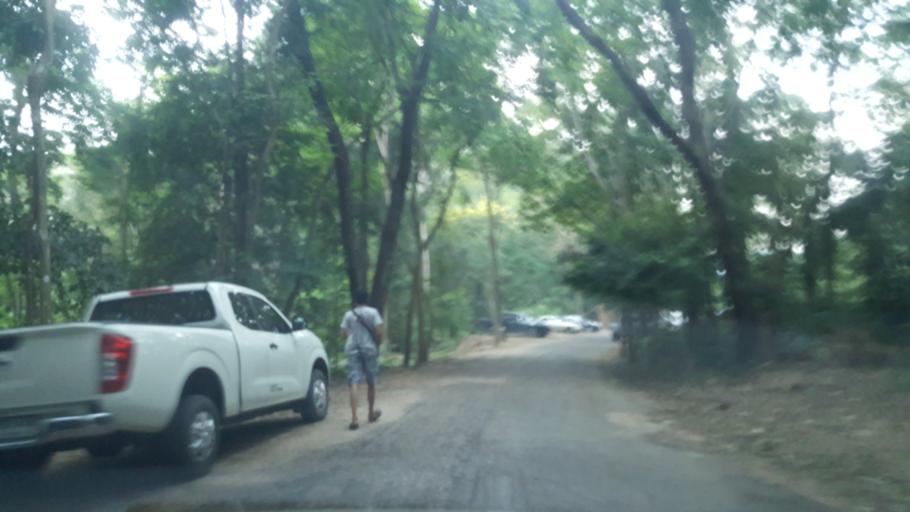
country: TH
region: Chon Buri
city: Ban Bueng
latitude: 13.2398
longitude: 101.0425
